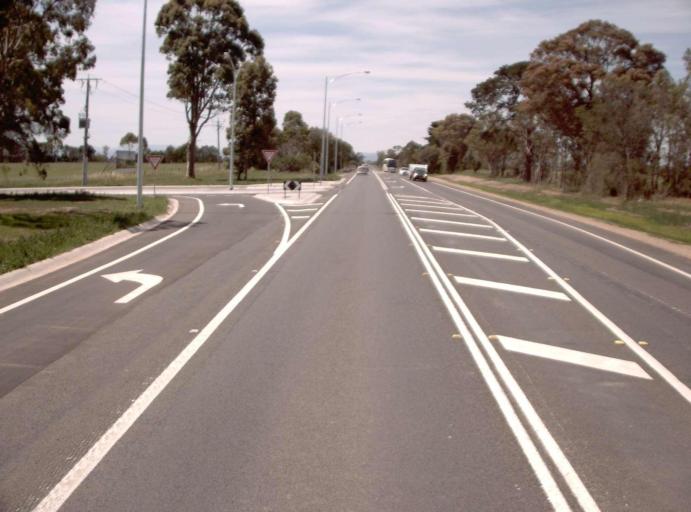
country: AU
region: Victoria
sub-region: Wellington
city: Sale
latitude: -38.0803
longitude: 147.0715
